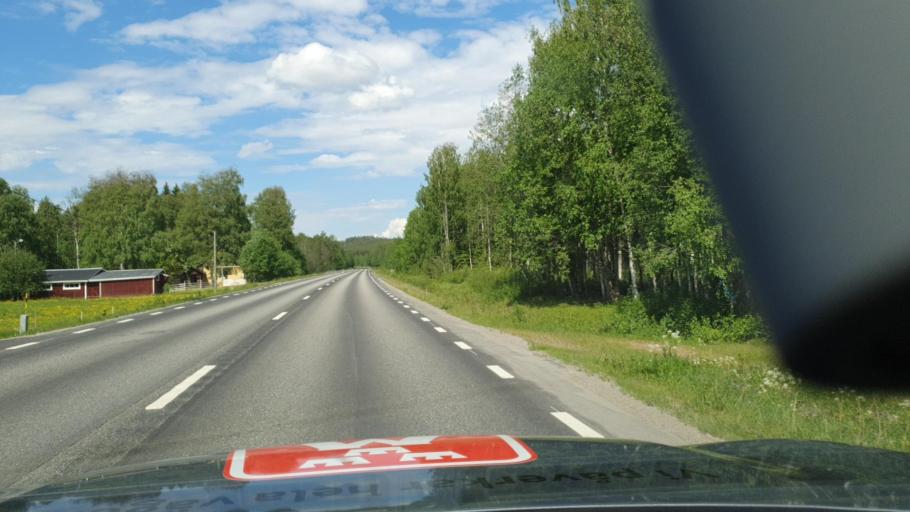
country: SE
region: Vaesternorrland
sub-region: Solleftea Kommun
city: As
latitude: 63.6244
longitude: 16.8172
